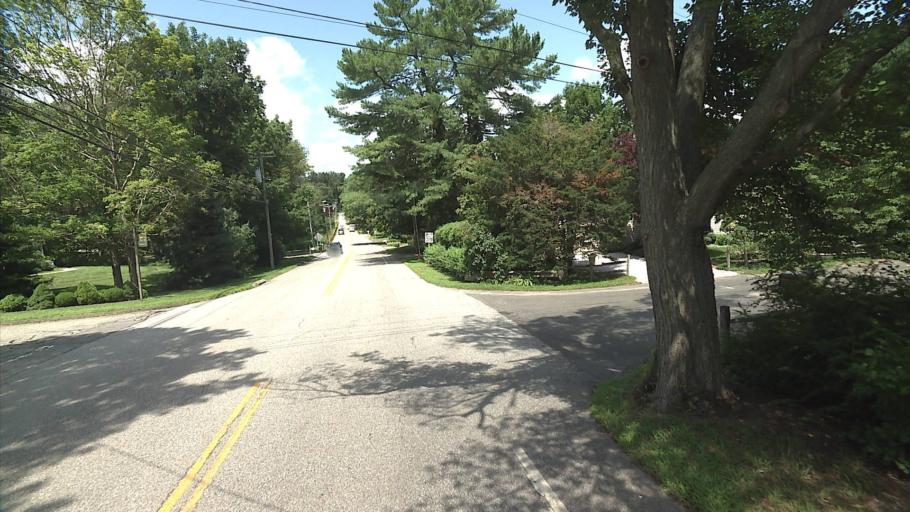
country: US
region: Connecticut
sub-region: Middlesex County
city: Essex Village
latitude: 41.3377
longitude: -72.3853
